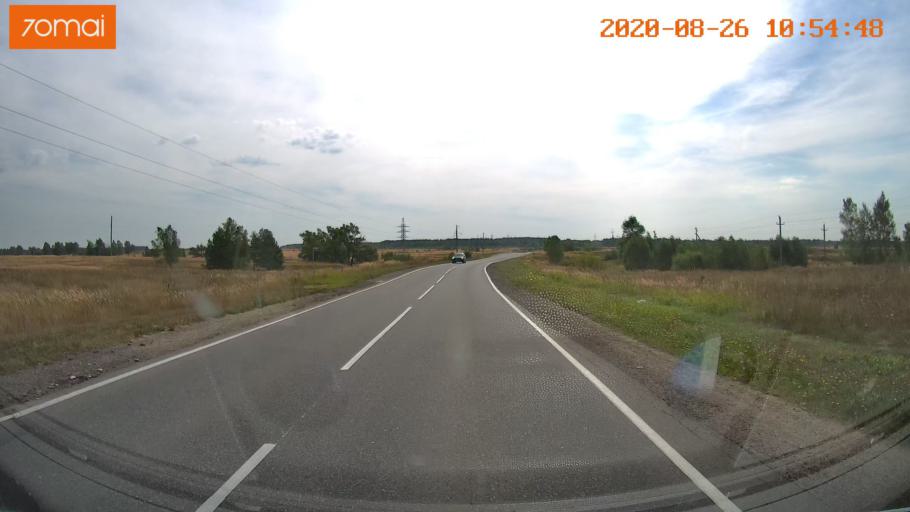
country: RU
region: Rjazan
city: Izhevskoye
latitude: 54.6258
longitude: 41.1664
